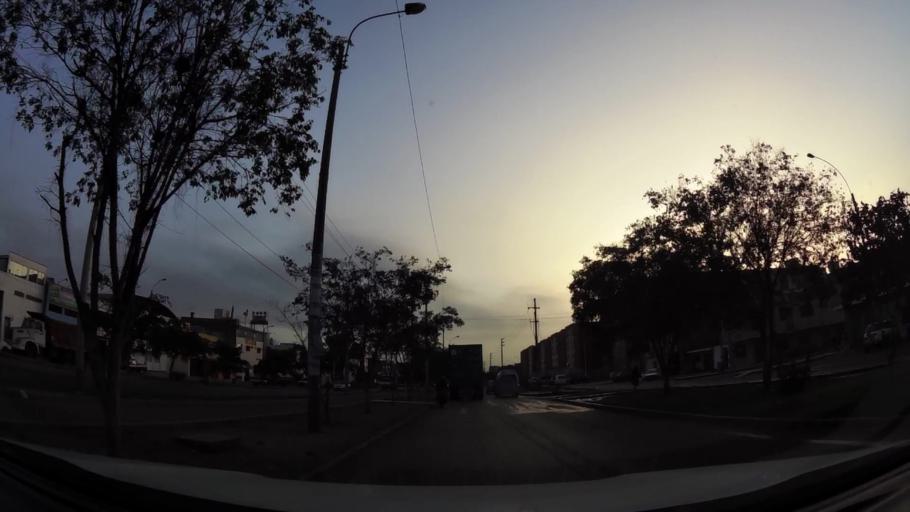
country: PE
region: Lima
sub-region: Lima
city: Independencia
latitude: -12.0116
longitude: -77.0737
